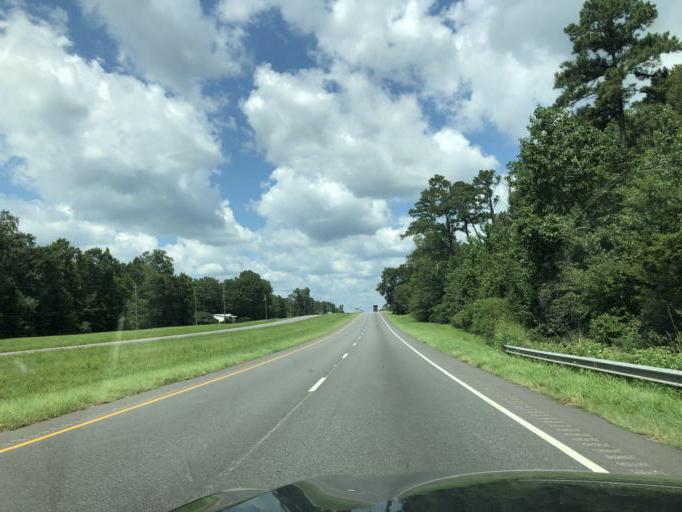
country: US
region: Alabama
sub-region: Barbour County
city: Eufaula
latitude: 31.9954
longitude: -85.1152
